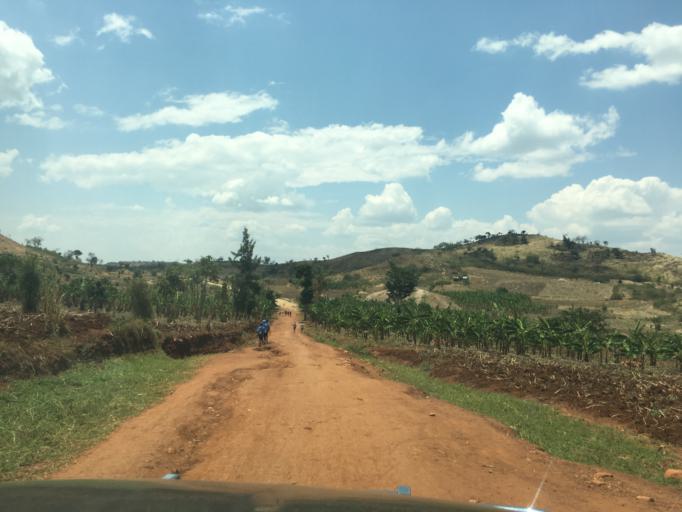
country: RW
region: Eastern Province
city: Kibungo
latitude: -2.1284
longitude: 30.8530
